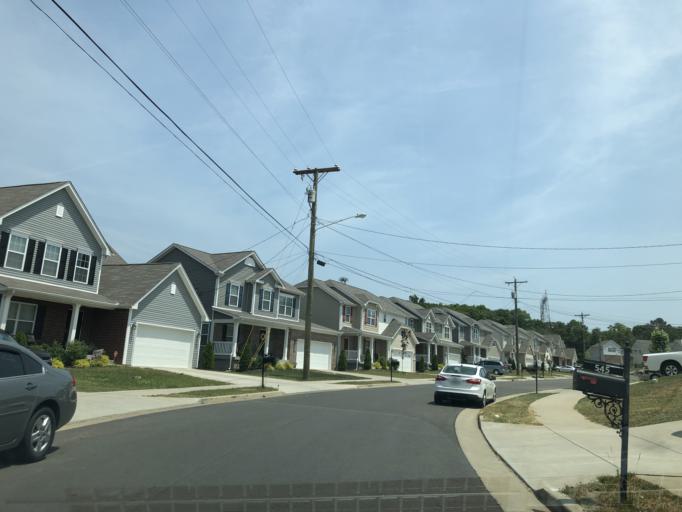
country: US
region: Tennessee
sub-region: Rutherford County
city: La Vergne
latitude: 36.0523
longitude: -86.6066
